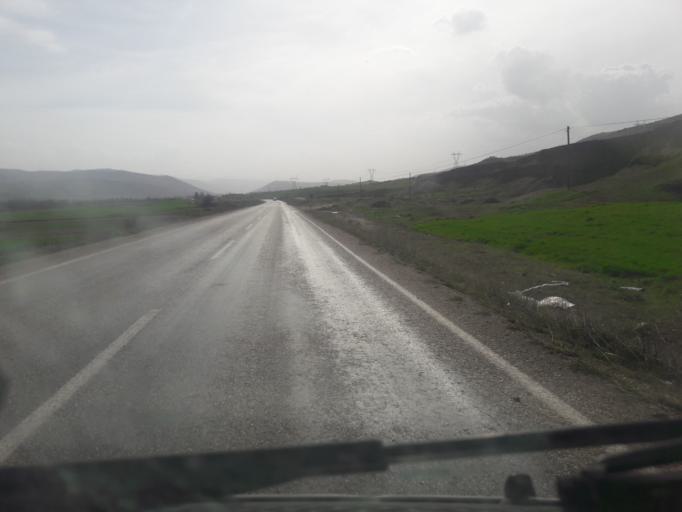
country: TR
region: Gumushane
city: Kelkit
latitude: 40.1397
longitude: 39.3905
